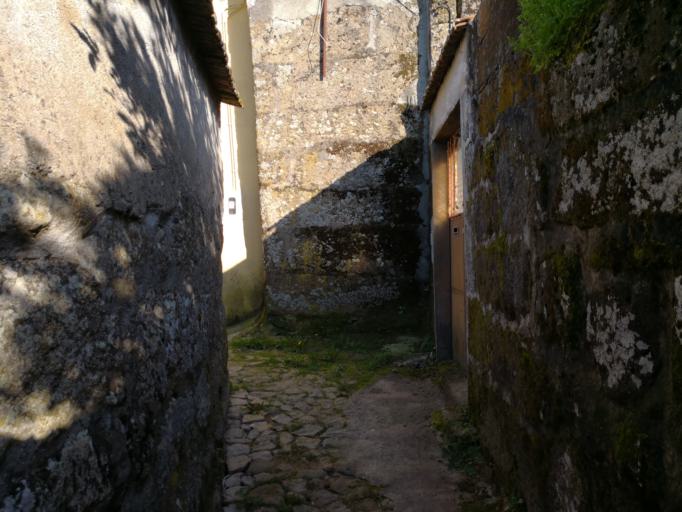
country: PT
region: Vila Real
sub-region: Vila Real
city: Vila Real
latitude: 41.2860
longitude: -7.7888
